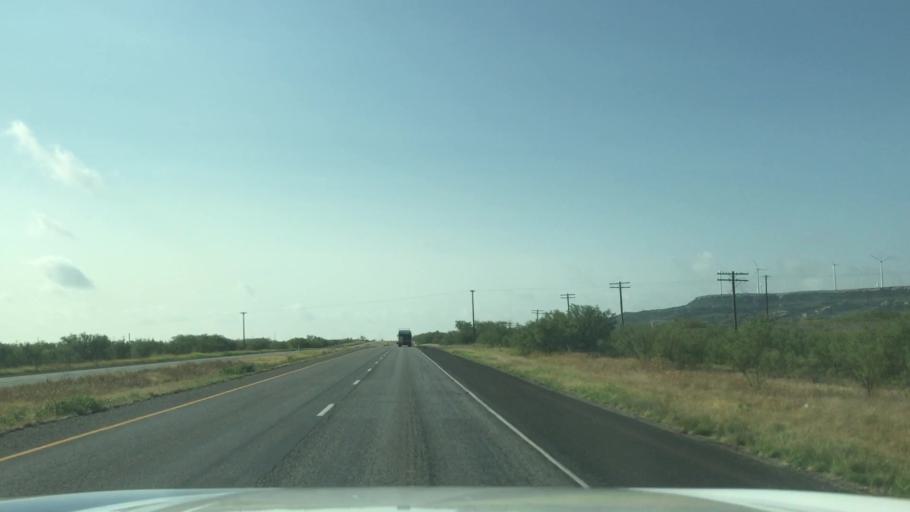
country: US
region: Texas
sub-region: Scurry County
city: Snyder
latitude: 32.9750
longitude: -101.1018
